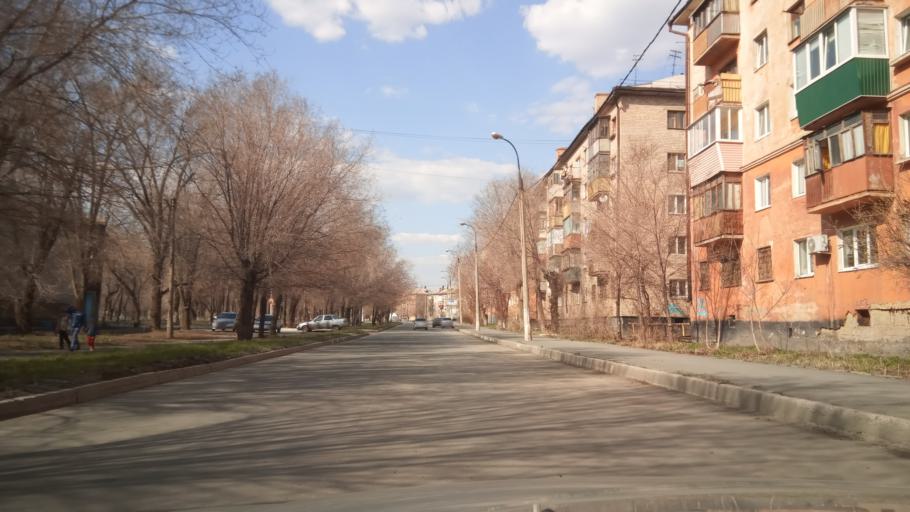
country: RU
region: Orenburg
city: Novotroitsk
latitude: 51.1944
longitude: 58.3014
